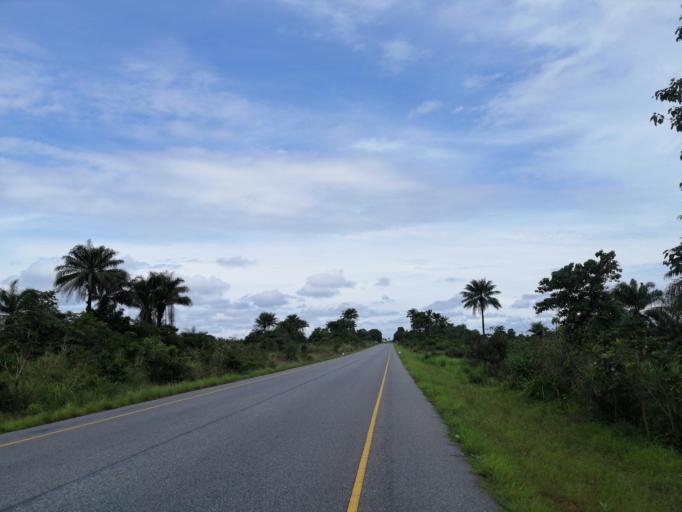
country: SL
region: Northern Province
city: Port Loko
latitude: 8.7393
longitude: -12.9430
